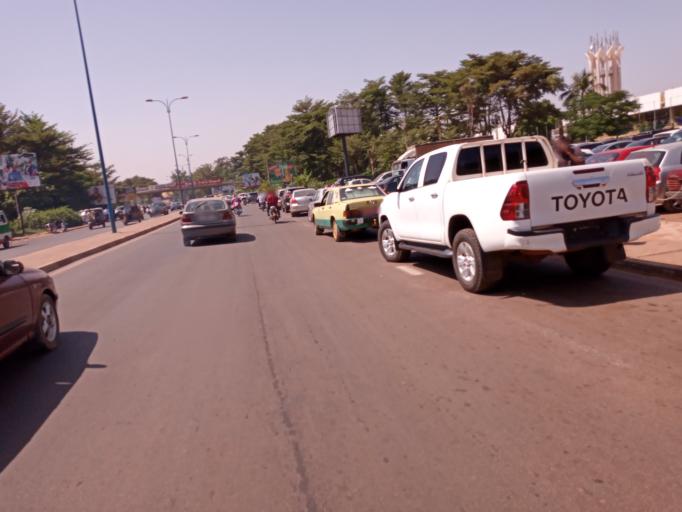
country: ML
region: Bamako
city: Bamako
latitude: 12.6298
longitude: -8.0045
